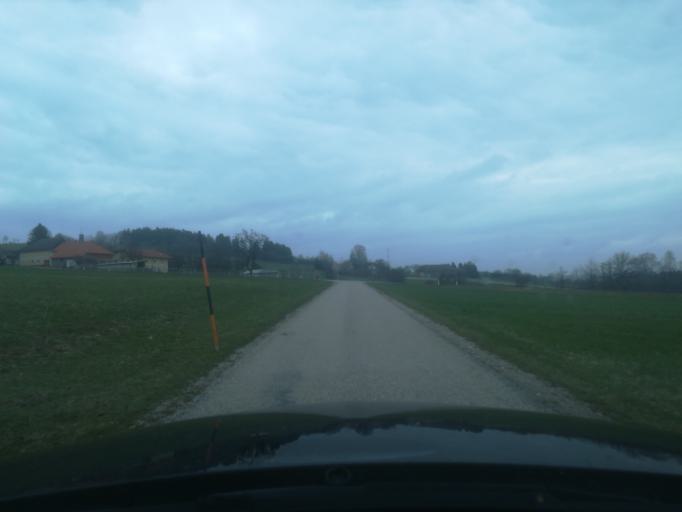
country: AT
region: Upper Austria
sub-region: Politischer Bezirk Rohrbach
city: Kleinzell im Muehlkreis
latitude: 48.3669
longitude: 13.9222
